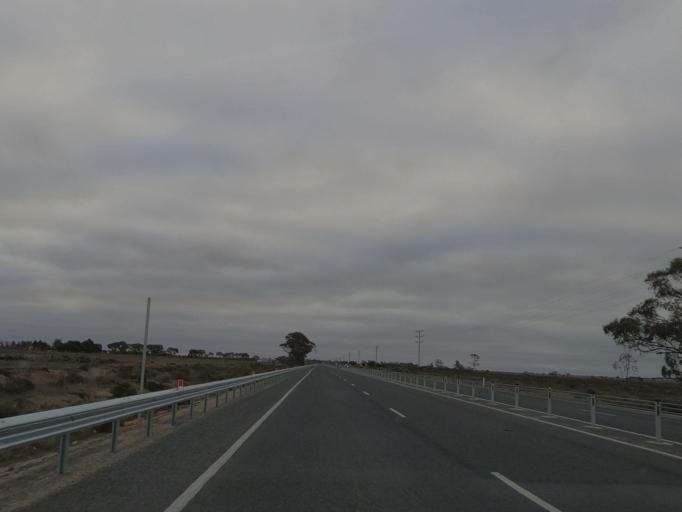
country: AU
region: Victoria
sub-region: Swan Hill
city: Swan Hill
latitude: -35.4784
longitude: 143.6866
